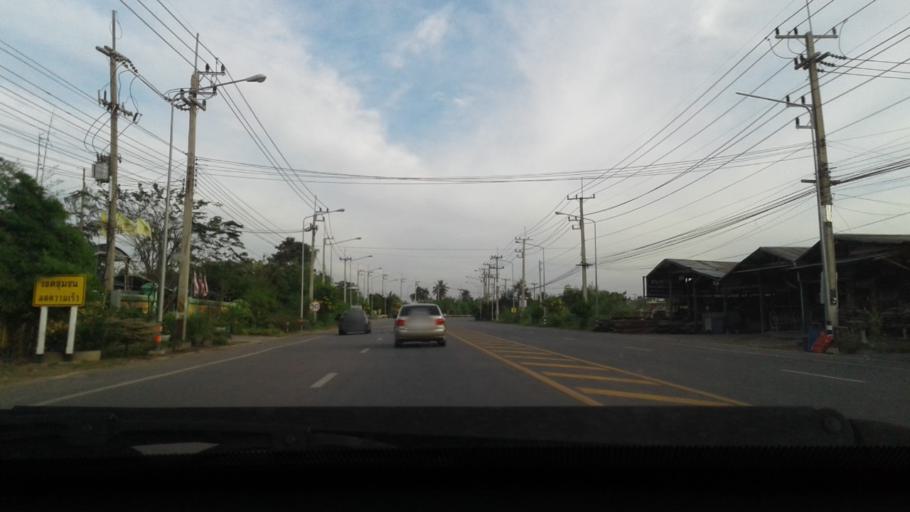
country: TH
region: Nonthaburi
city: Sai Noi
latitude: 13.9311
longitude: 100.2443
